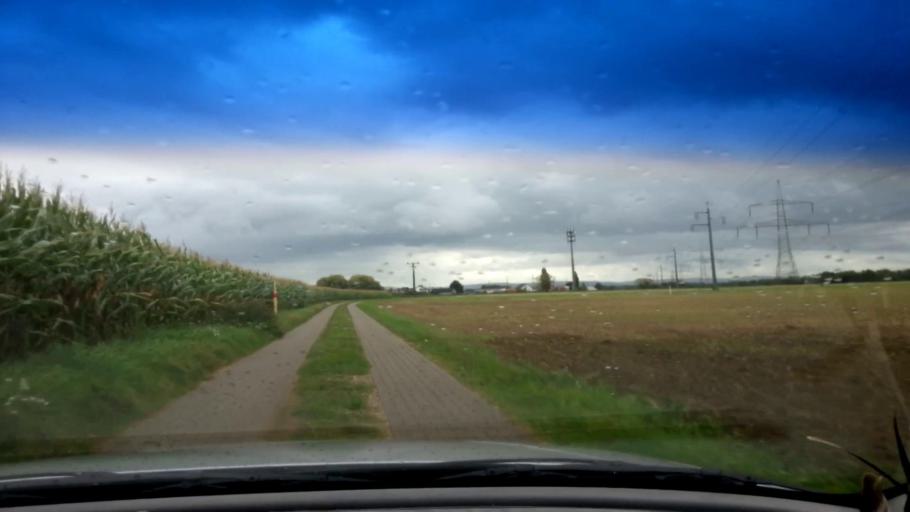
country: DE
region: Bavaria
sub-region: Upper Franconia
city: Oberhaid
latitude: 49.9293
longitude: 10.8051
